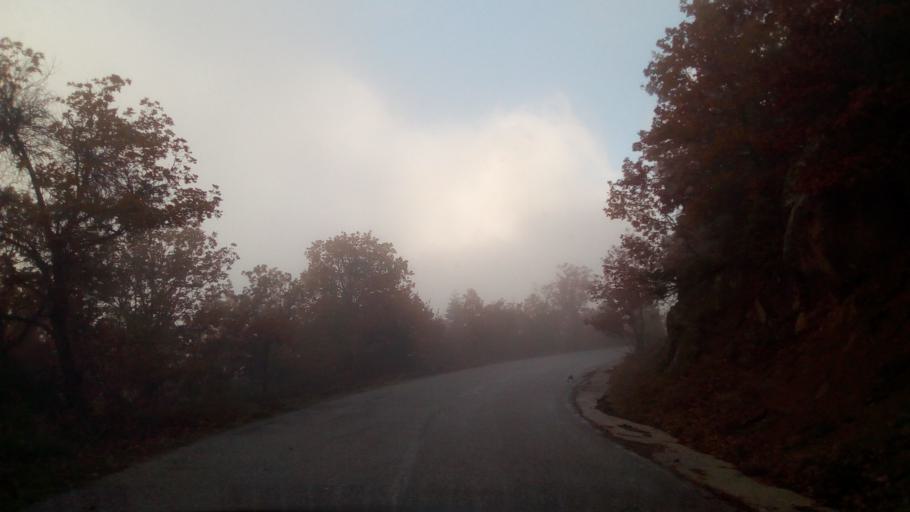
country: GR
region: West Greece
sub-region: Nomos Aitolias kai Akarnanias
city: Nafpaktos
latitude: 38.5567
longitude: 21.9282
